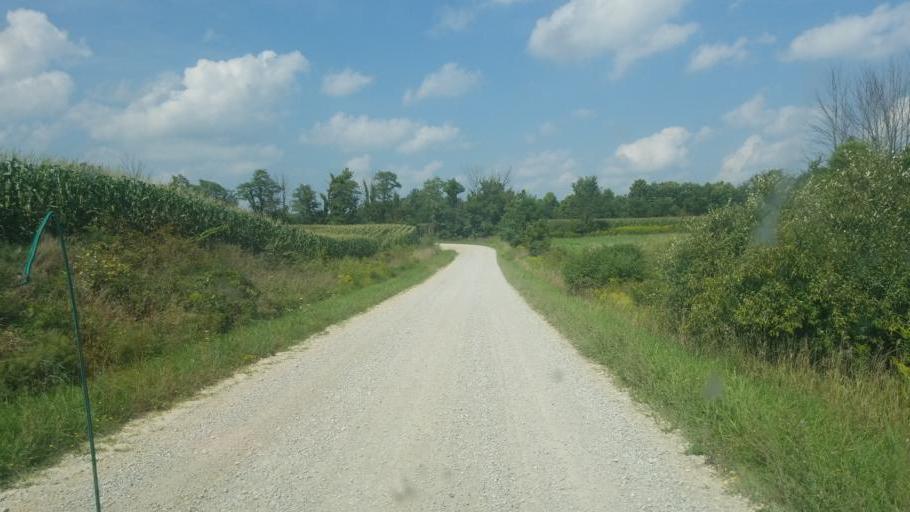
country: US
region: Ohio
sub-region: Huron County
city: New London
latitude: 40.9850
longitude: -82.4082
